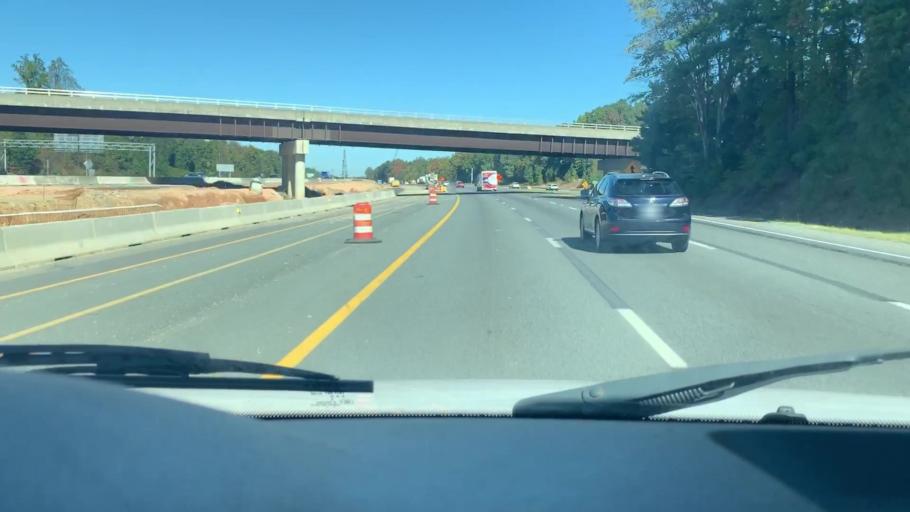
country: US
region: North Carolina
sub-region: Mecklenburg County
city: Huntersville
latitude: 35.3674
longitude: -80.8424
